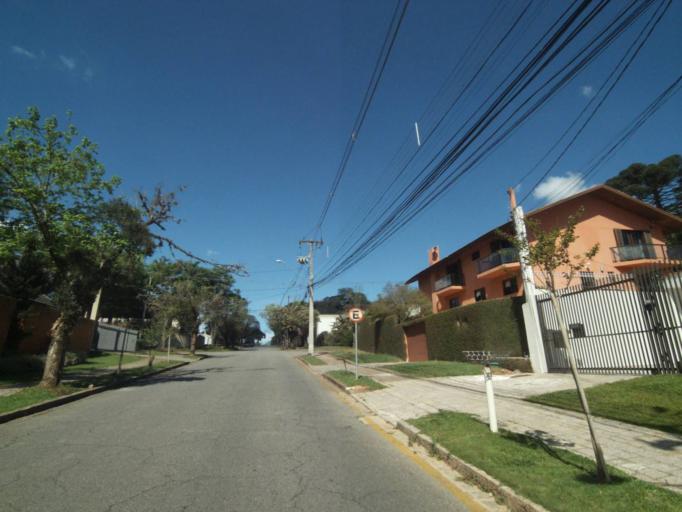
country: BR
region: Parana
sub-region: Curitiba
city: Curitiba
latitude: -25.3987
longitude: -49.2665
